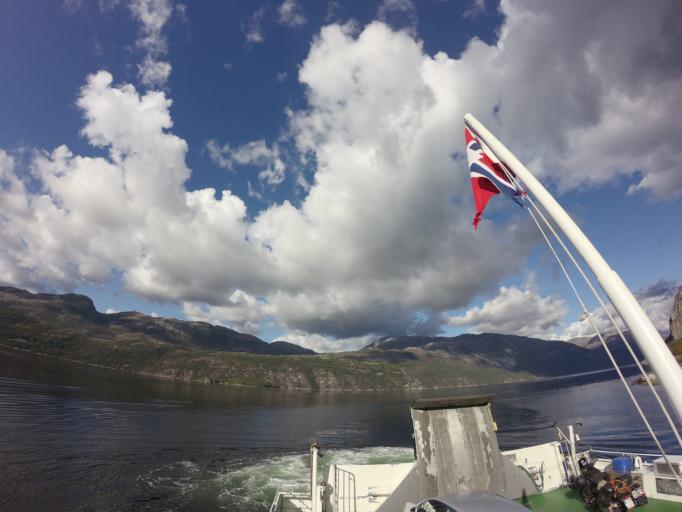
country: NO
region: Rogaland
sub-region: Forsand
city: Forsand
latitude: 59.0094
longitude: 6.3939
